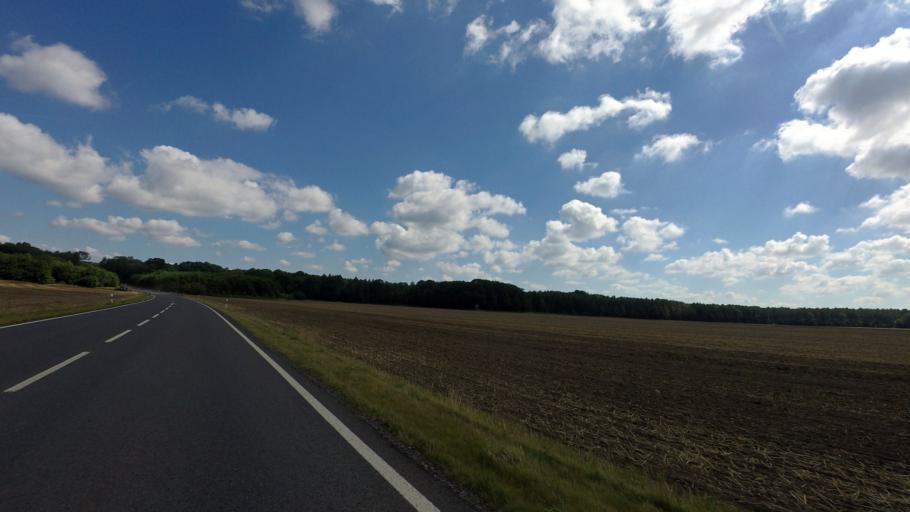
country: DE
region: Saxony
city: Bernsdorf
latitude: 51.3554
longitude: 14.0797
